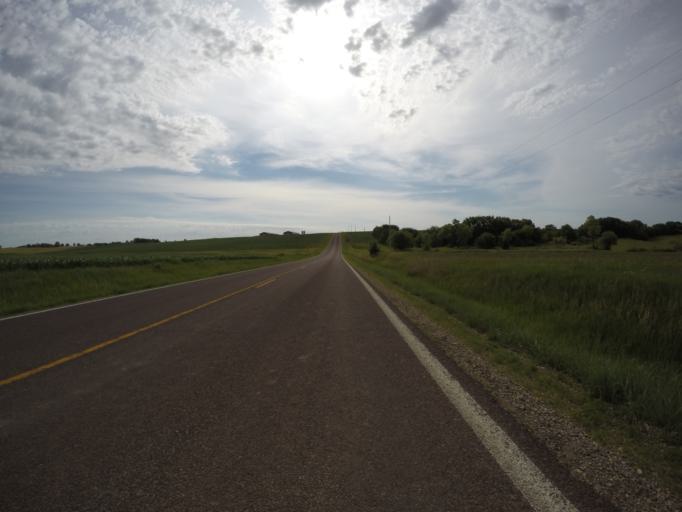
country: US
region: Kansas
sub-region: Washington County
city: Washington
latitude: 39.7121
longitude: -97.3378
